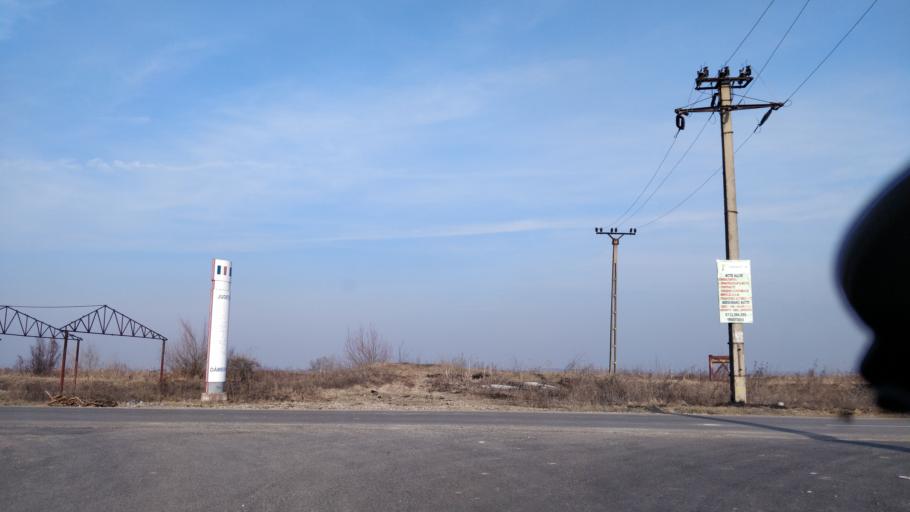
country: RO
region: Giurgiu
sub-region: Comuna Cosoba
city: Cosoba
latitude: 44.5394
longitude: 25.8021
